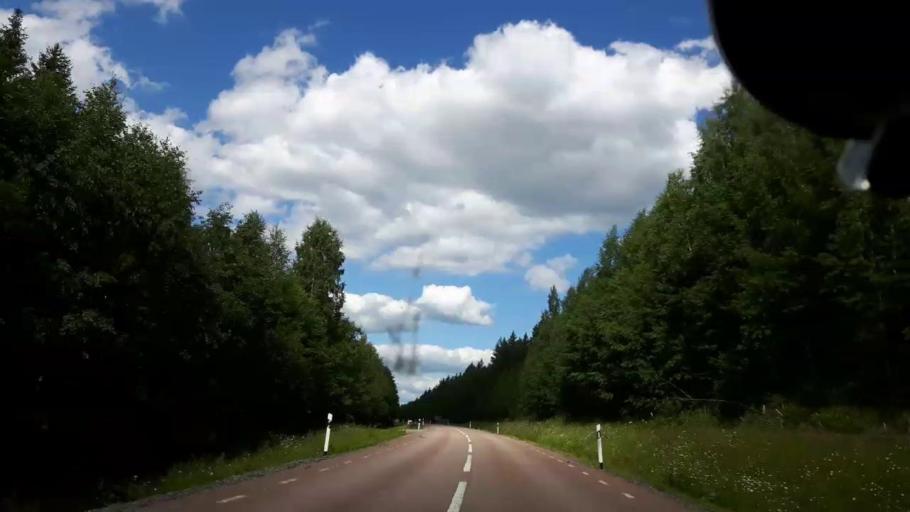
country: SE
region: Jaemtland
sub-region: Ragunda Kommun
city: Hammarstrand
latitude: 62.9217
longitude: 16.7034
